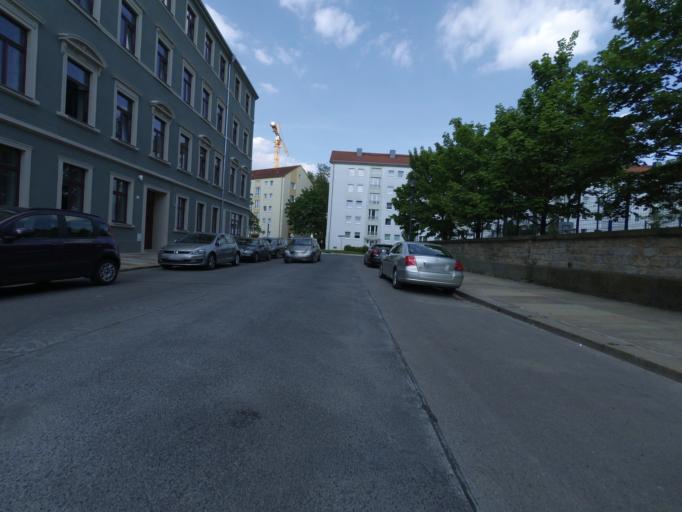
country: DE
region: Saxony
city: Dresden
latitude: 51.0519
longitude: 13.7235
